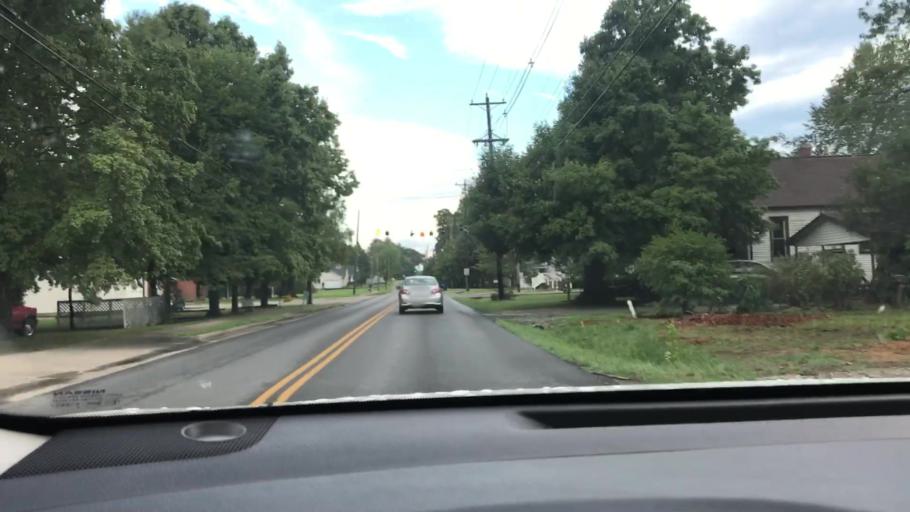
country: US
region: Kentucky
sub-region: Calloway County
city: Murray
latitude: 36.6073
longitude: -88.3245
